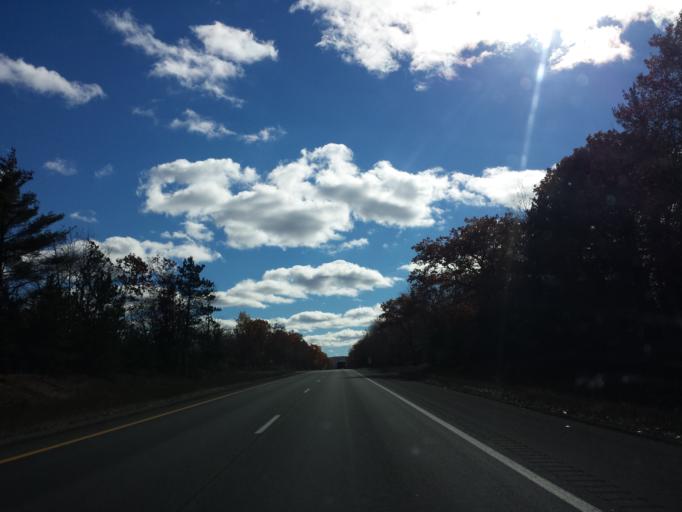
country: US
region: Michigan
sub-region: Cheboygan County
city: Indian River
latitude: 45.3931
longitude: -84.6073
